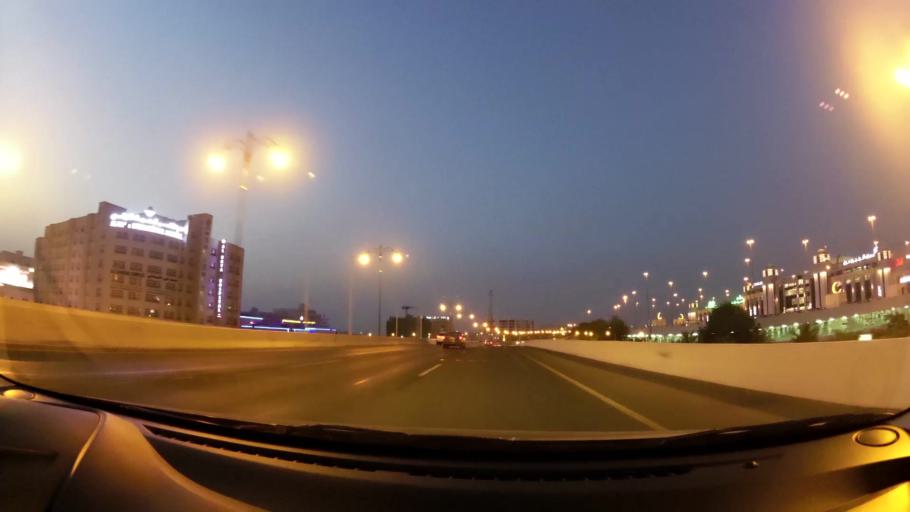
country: OM
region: Muhafazat Masqat
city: Bawshar
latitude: 23.5889
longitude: 58.4079
